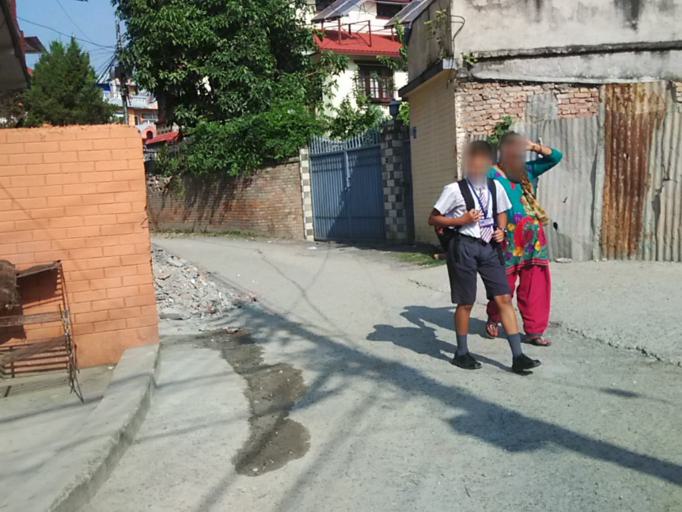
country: NP
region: Central Region
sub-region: Bagmati Zone
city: Kathmandu
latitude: 27.7356
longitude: 85.3407
